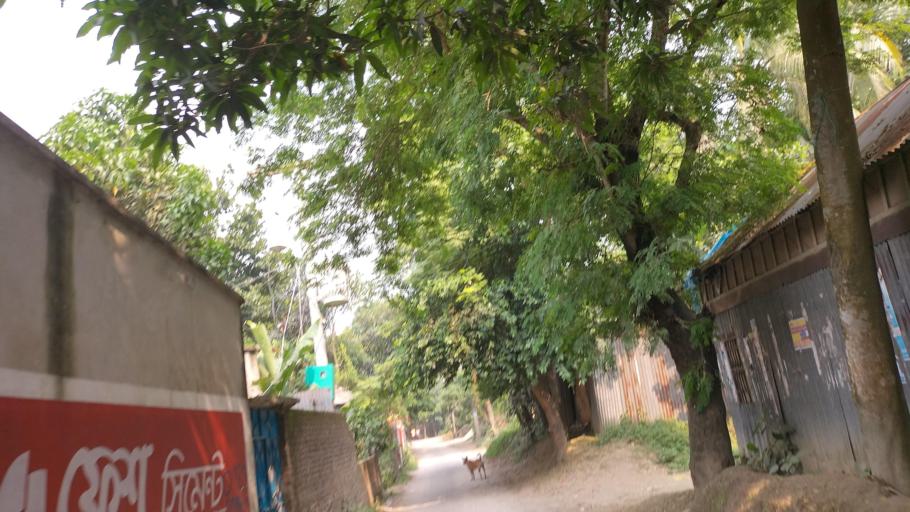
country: BD
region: Dhaka
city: Azimpur
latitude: 23.6897
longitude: 90.3022
